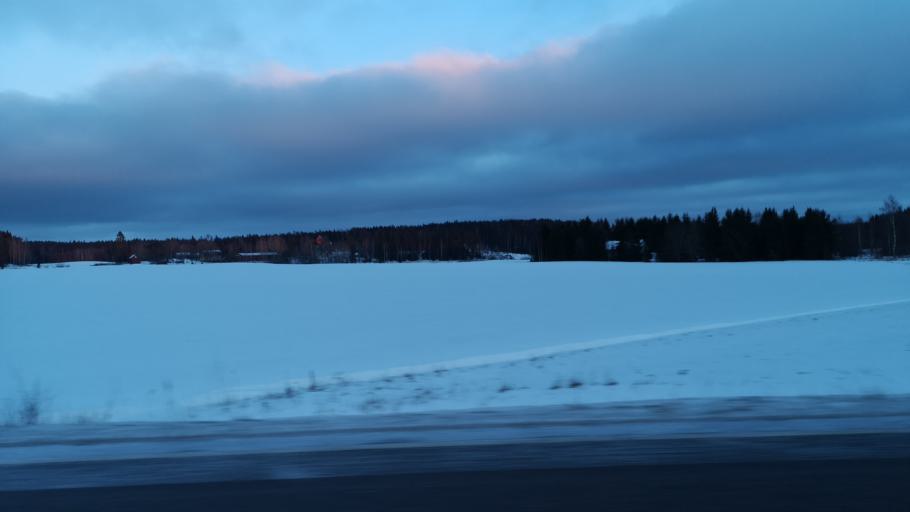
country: FI
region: Uusimaa
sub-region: Raaseporin
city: Inga
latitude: 60.1138
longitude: 23.8822
